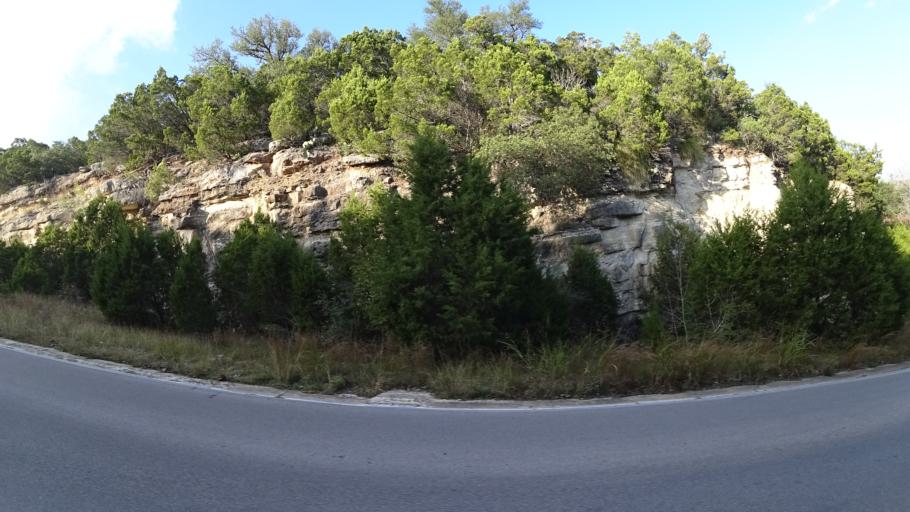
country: US
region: Texas
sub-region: Travis County
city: Lost Creek
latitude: 30.2715
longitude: -97.8474
